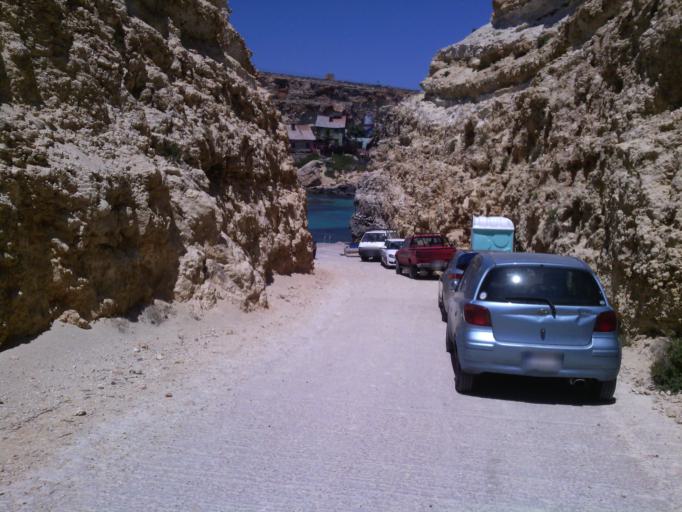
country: MT
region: Il-Mellieha
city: Mellieha
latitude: 35.9592
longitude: 14.3404
